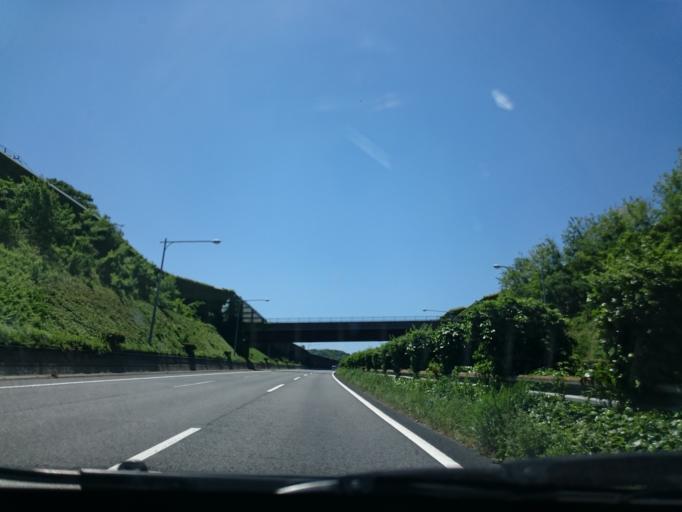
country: JP
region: Kanagawa
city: Hadano
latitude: 35.3630
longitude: 139.2553
